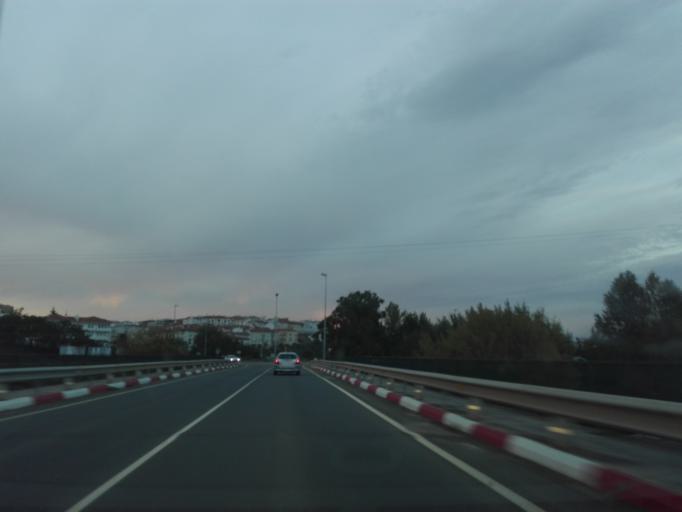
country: ES
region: Extremadura
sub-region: Provincia de Caceres
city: Coria
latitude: 39.9797
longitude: -6.5284
